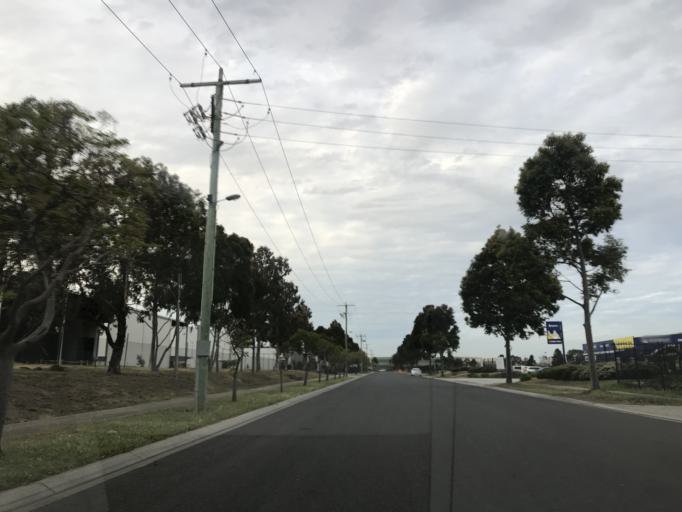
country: AU
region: Victoria
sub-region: Brimbank
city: Derrimut
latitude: -37.8087
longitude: 144.7814
